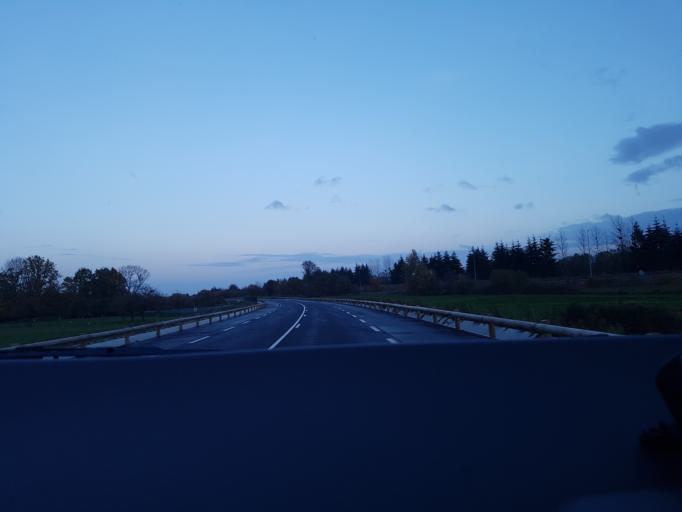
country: FR
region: Haute-Normandie
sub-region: Departement de l'Eure
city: Beuzeville
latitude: 49.3259
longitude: 0.3307
